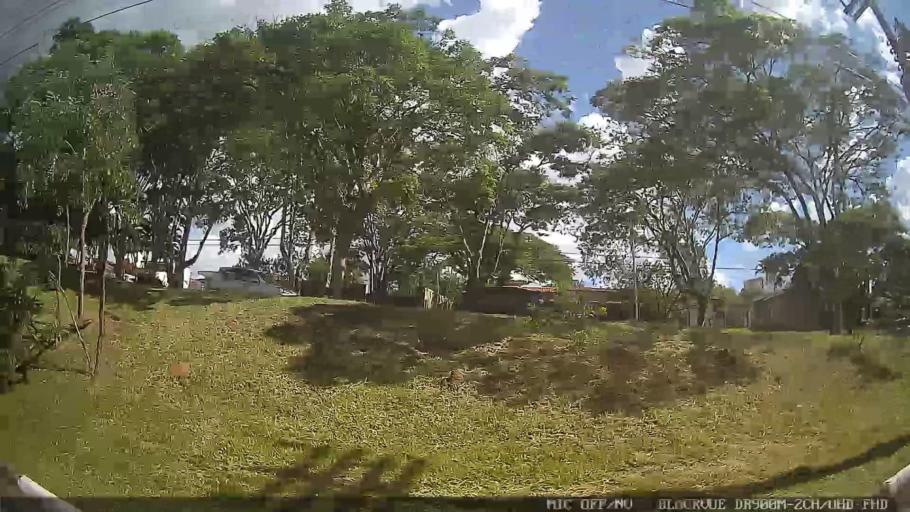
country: BR
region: Sao Paulo
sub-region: Atibaia
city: Atibaia
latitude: -23.1139
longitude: -46.5426
